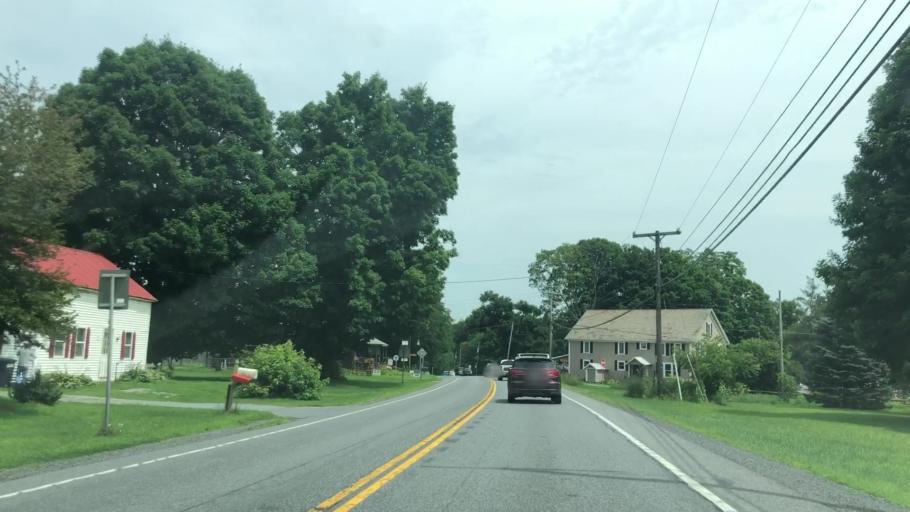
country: US
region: New York
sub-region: Warren County
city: Queensbury
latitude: 43.4079
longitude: -73.5677
